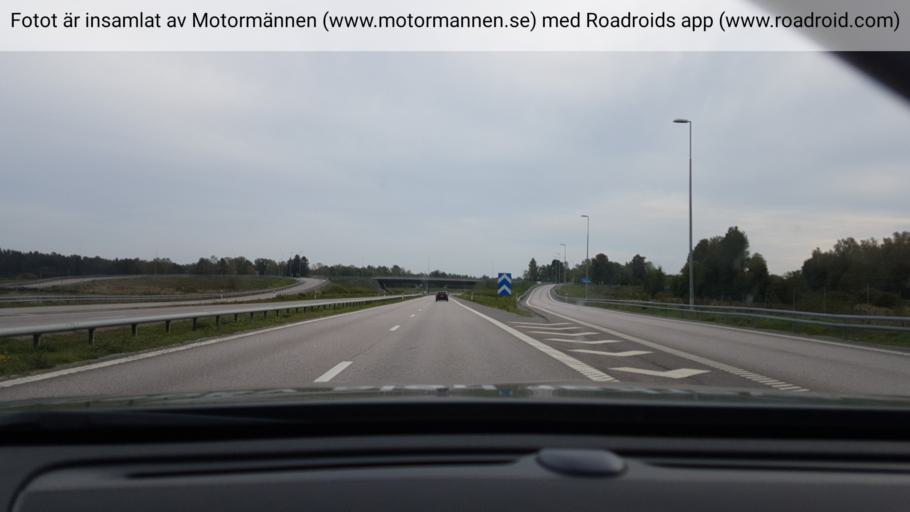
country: SE
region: Stockholm
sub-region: Nynashamns Kommun
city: Osmo
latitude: 58.9455
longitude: 17.9091
